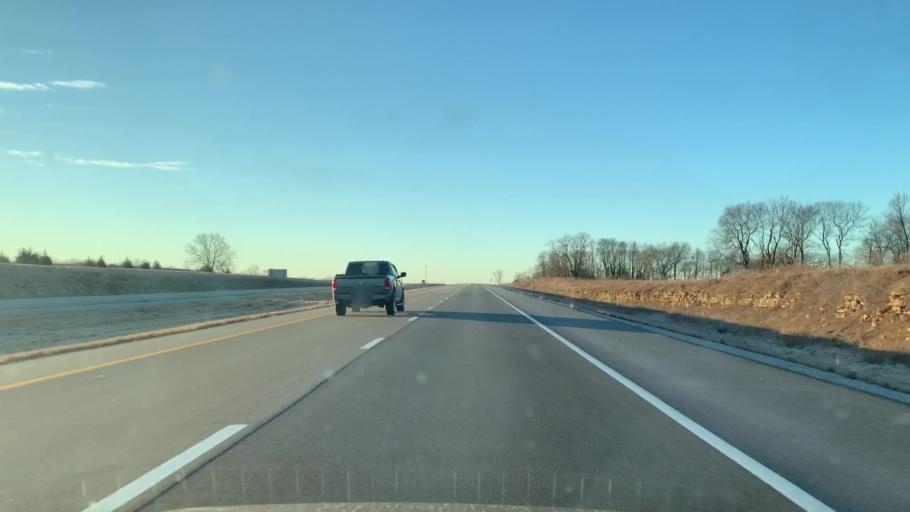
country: US
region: Kansas
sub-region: Linn County
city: La Cygne
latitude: 38.3845
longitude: -94.6877
